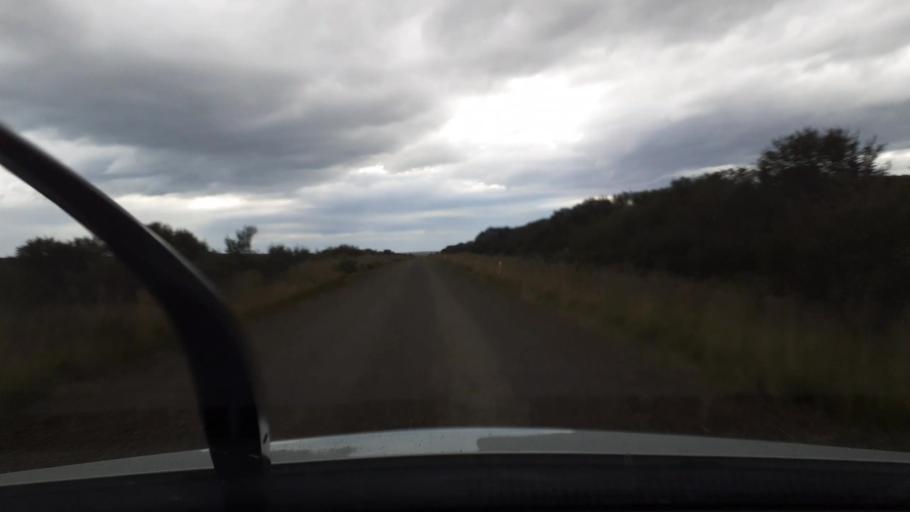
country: IS
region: West
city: Borgarnes
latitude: 64.6046
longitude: -21.9676
